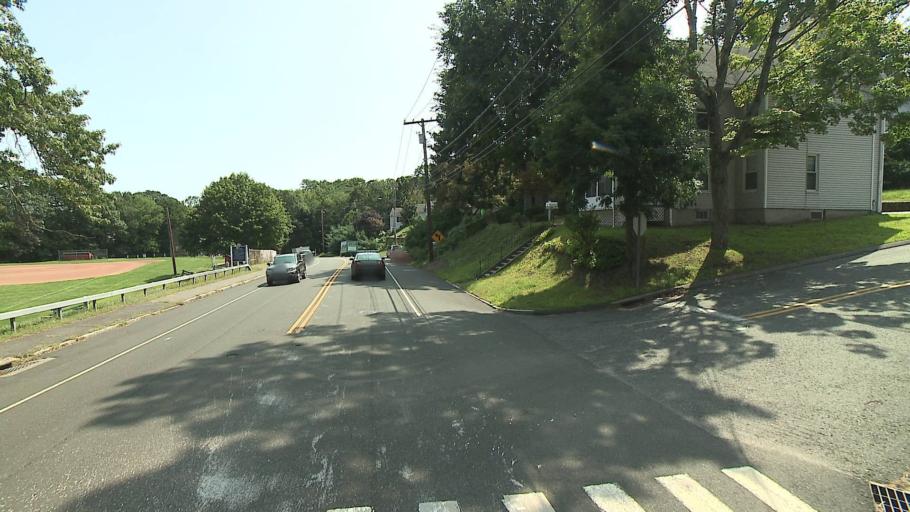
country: US
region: Connecticut
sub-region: Fairfield County
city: Shelton
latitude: 41.3218
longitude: -73.1011
